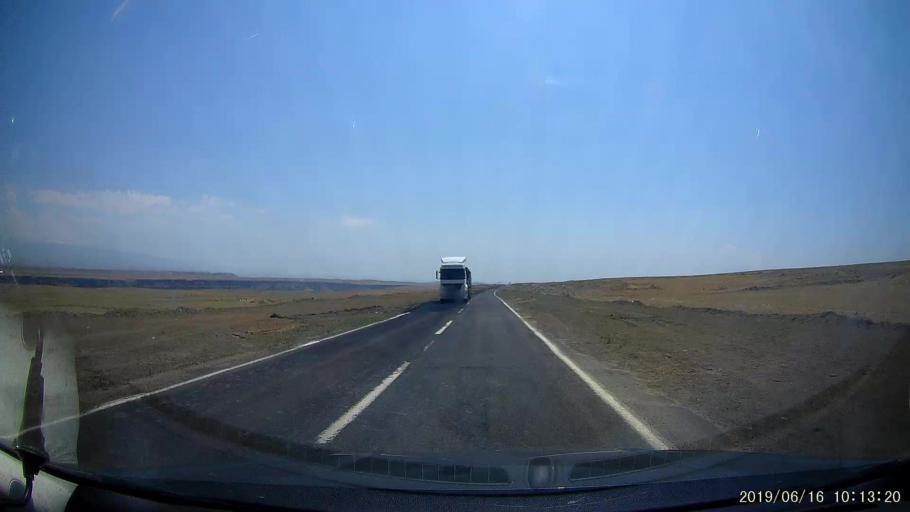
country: TR
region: Igdir
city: Tuzluca
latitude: 40.1931
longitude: 43.6402
